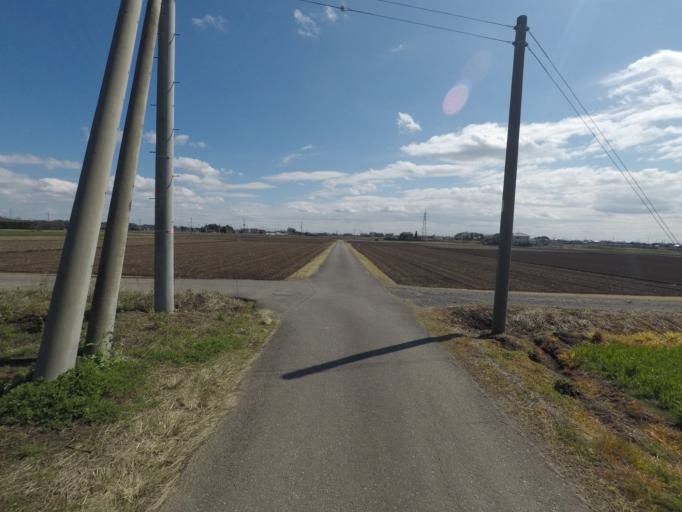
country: JP
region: Ibaraki
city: Moriya
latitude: 35.9659
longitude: 140.0427
